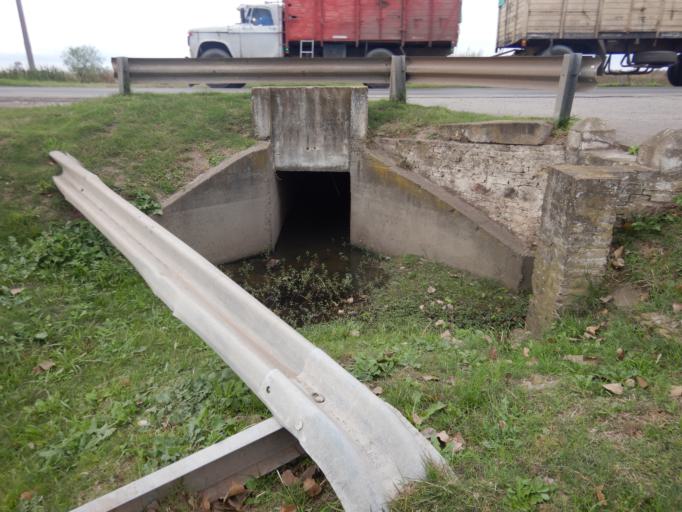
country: AR
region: Santa Fe
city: Roldan
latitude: -32.9000
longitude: -60.9387
